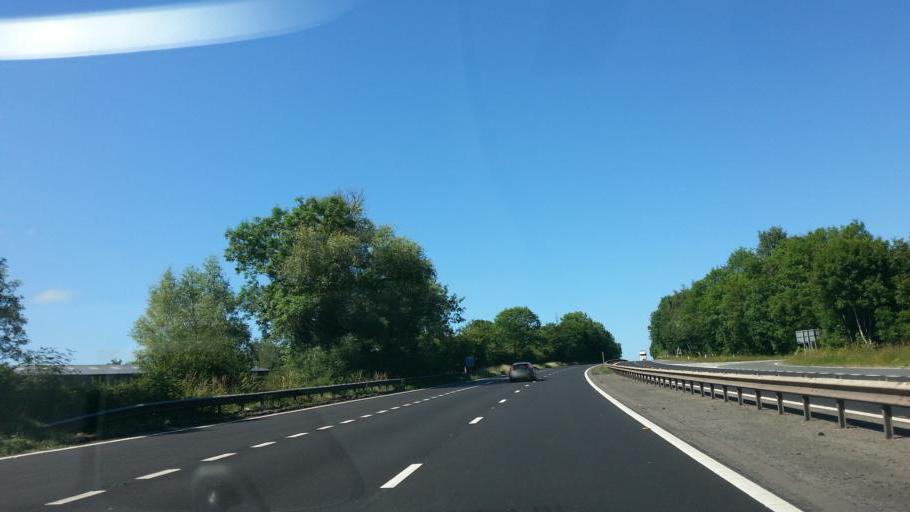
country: GB
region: England
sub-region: Herefordshire
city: Linton
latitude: 51.9335
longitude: -2.4845
